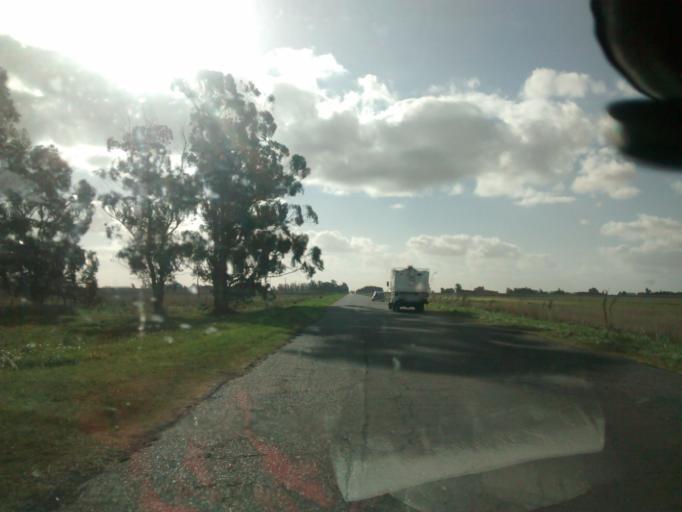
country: AR
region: Buenos Aires
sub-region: Partido de Ayacucho
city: Ayacucho
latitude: -37.1729
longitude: -58.5226
